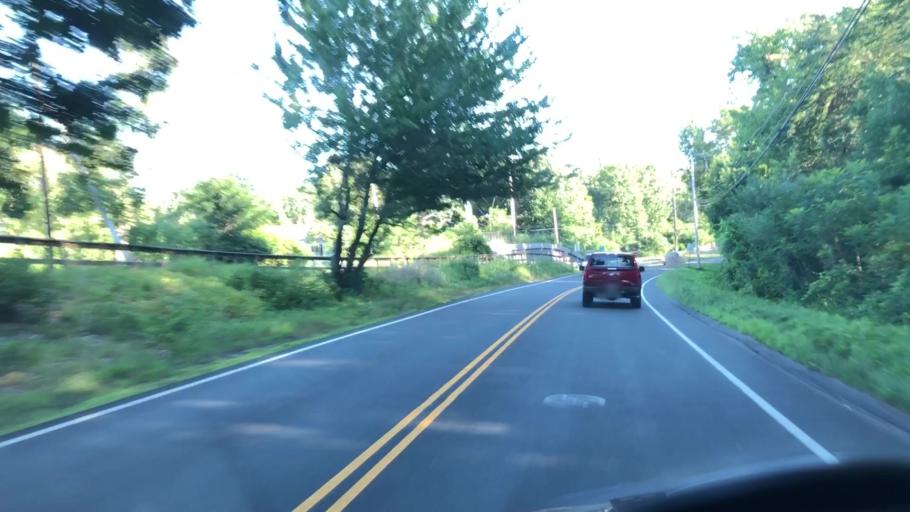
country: US
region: Massachusetts
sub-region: Hampshire County
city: Easthampton
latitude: 42.2820
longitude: -72.6539
